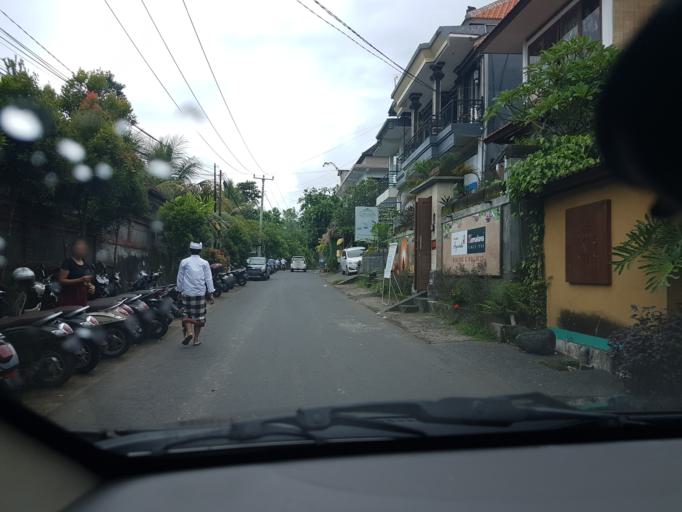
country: ID
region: Bali
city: Banjar Pande
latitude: -8.5037
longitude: 115.2475
